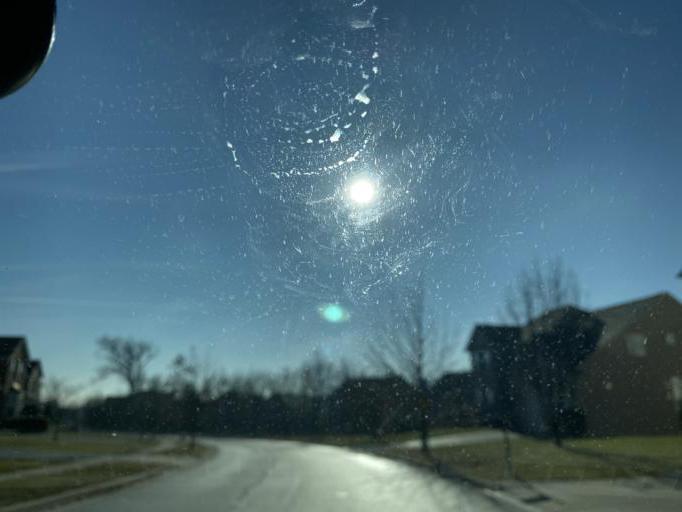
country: US
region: Maryland
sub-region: Prince George's County
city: South Laurel
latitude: 39.0828
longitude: -76.8762
